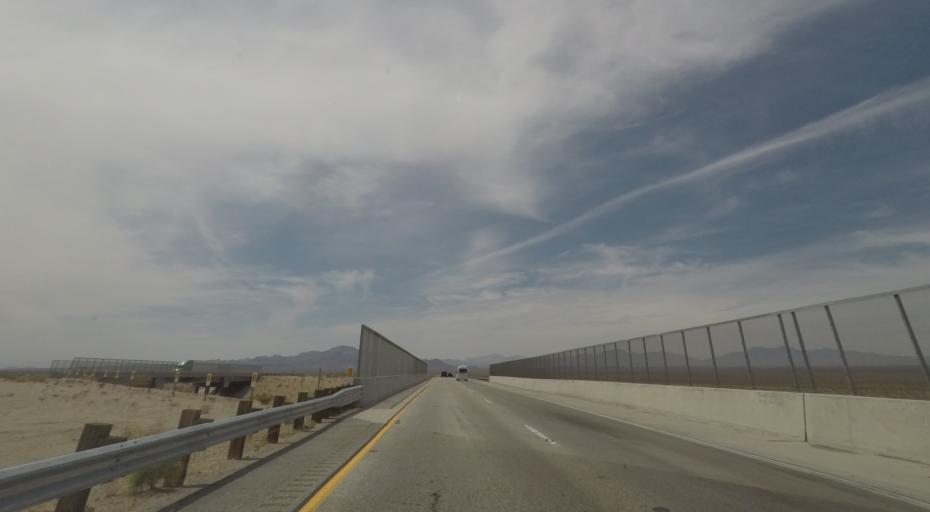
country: US
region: California
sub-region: San Bernardino County
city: Needles
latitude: 34.8134
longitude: -115.1828
